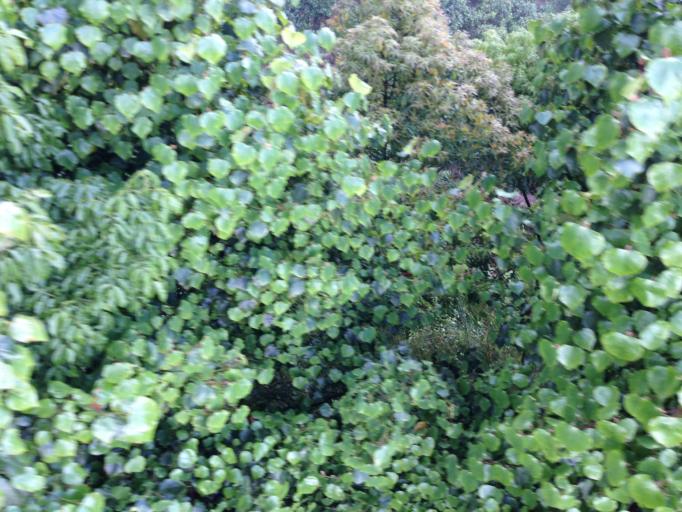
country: IN
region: West Bengal
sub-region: Darjiling
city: Darjiling
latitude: 27.0700
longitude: 88.2546
